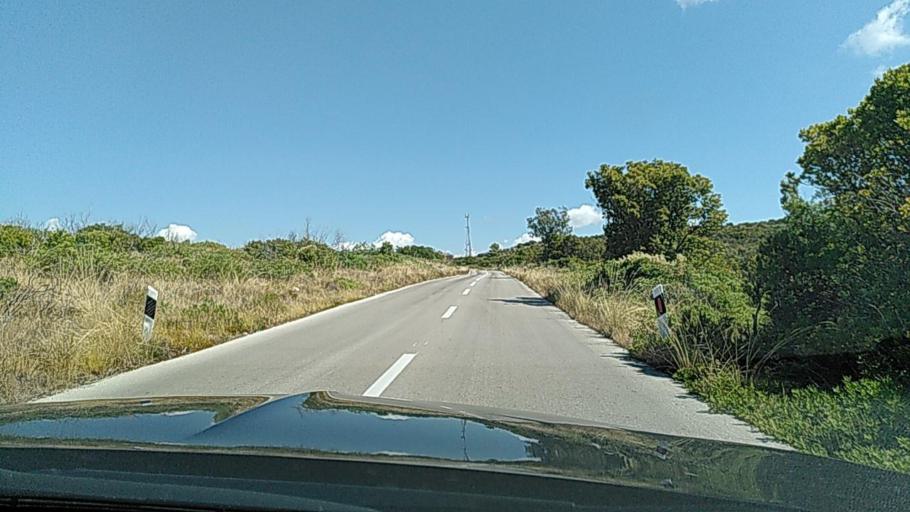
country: HR
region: Dubrovacko-Neretvanska
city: Orebic
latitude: 43.1254
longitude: 17.1225
